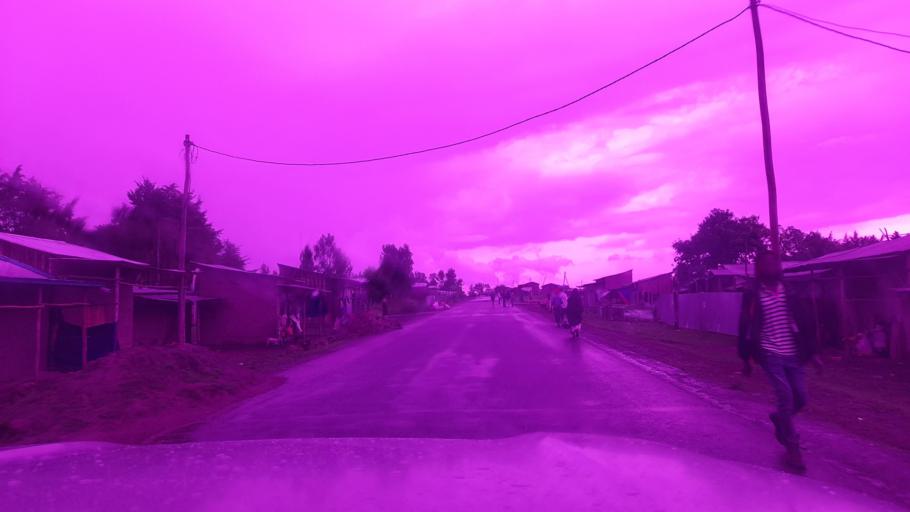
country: ET
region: Oromiya
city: Jima
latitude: 7.7147
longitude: 37.0949
